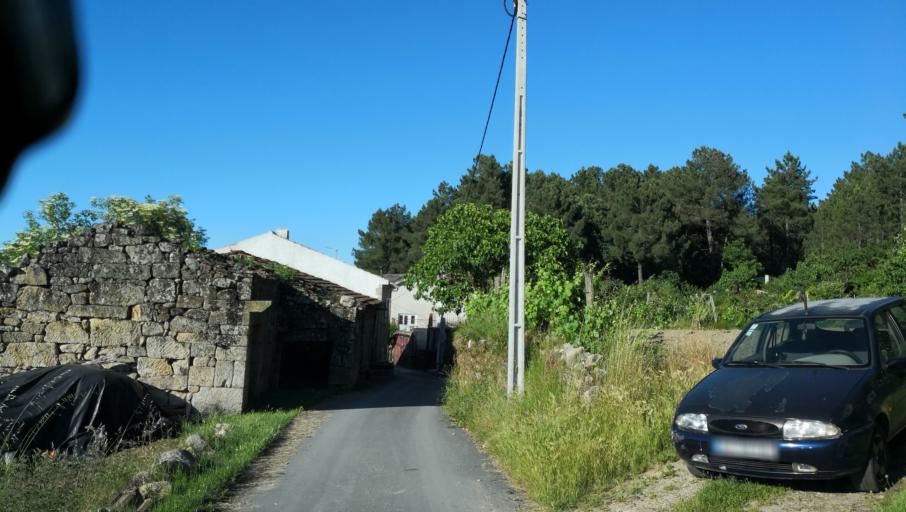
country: PT
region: Vila Real
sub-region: Vila Real
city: Vila Real
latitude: 41.3219
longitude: -7.6754
